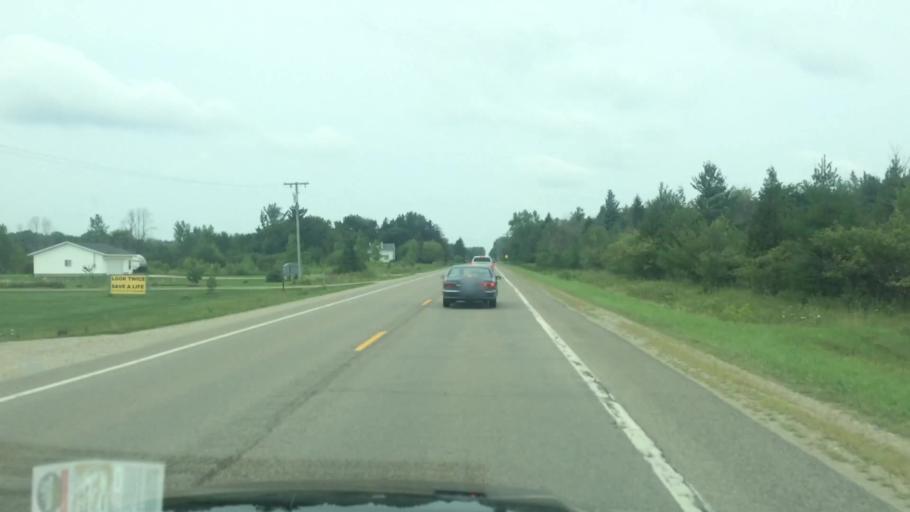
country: US
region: Michigan
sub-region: Huron County
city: Bad Axe
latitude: 43.8840
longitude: -83.0029
